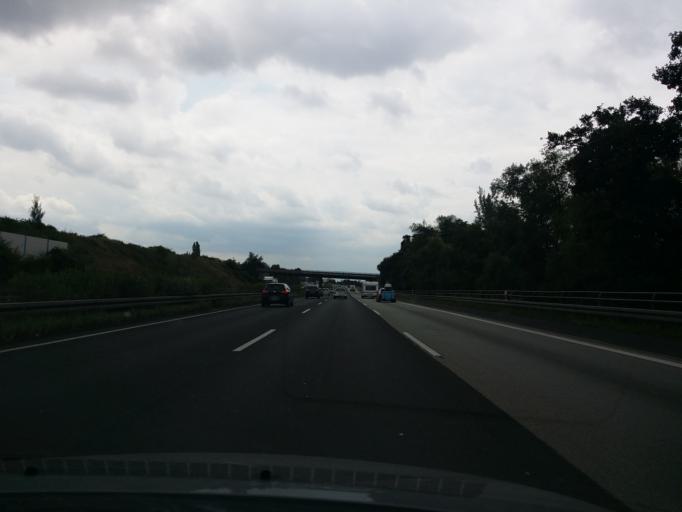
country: DE
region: Hesse
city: Eppstein
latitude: 50.0820
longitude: 8.3617
